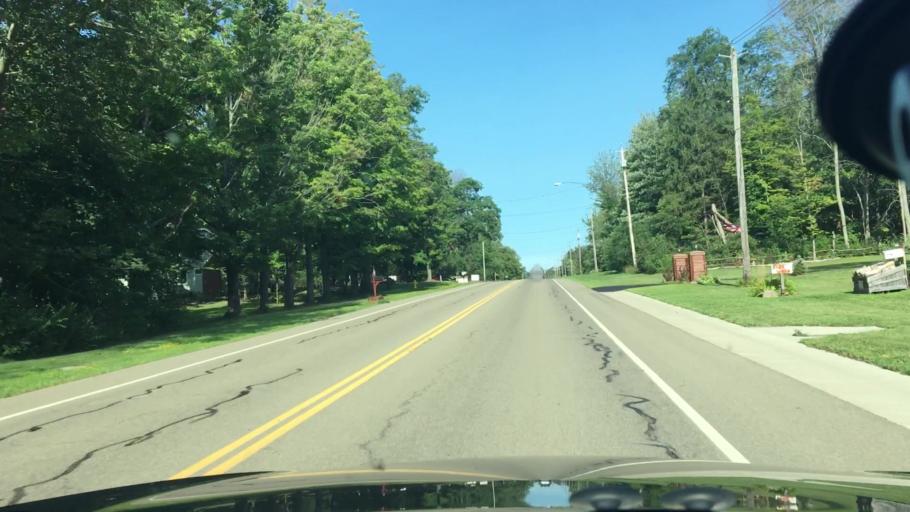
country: US
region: New York
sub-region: Erie County
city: Angola
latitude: 42.6524
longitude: -79.0206
